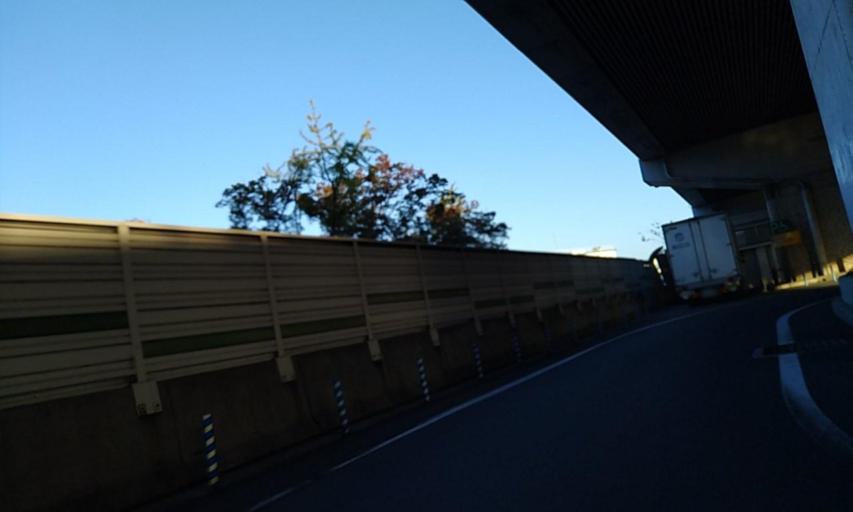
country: JP
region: Osaka
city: Daitocho
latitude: 34.6888
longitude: 135.5939
